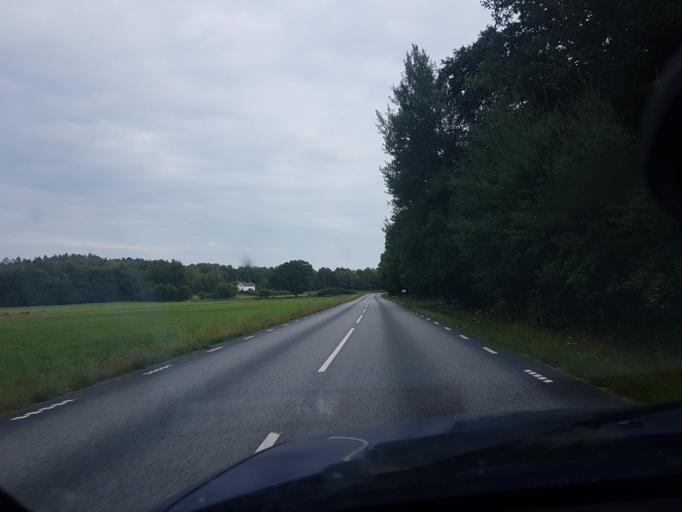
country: SE
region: Vaestra Goetaland
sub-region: Lysekils Kommun
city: Lysekil
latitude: 58.2680
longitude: 11.5366
